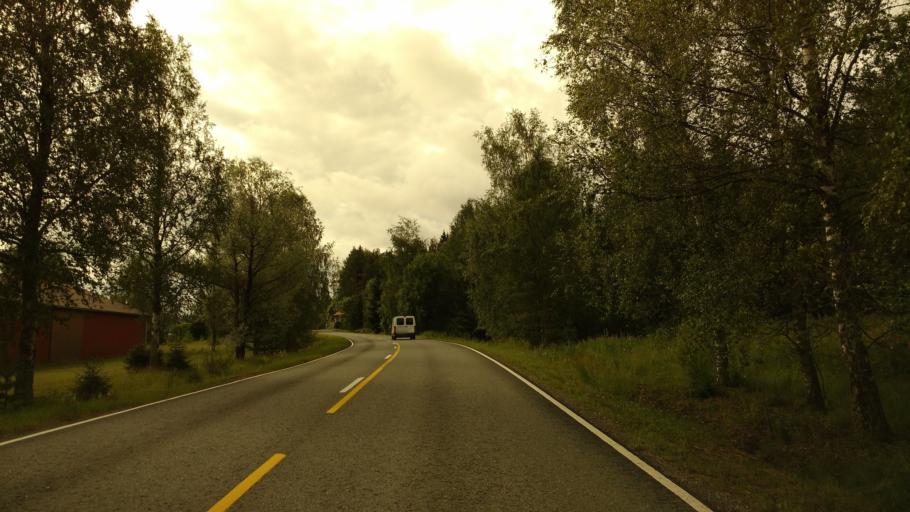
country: FI
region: Varsinais-Suomi
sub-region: Salo
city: Kuusjoki
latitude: 60.5268
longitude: 23.1725
